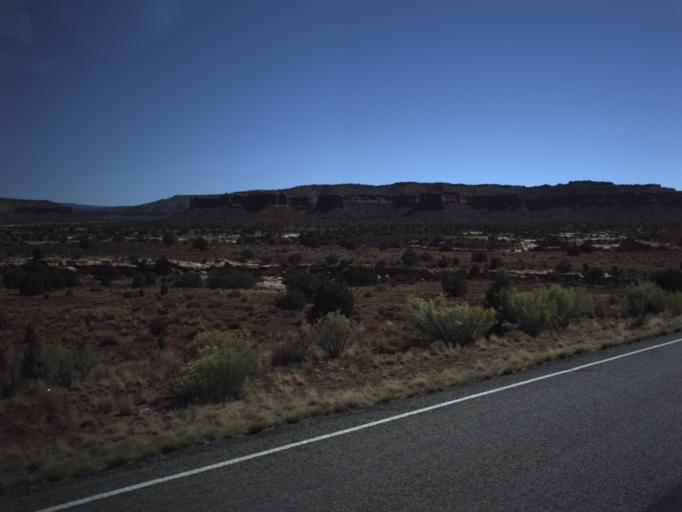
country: US
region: Utah
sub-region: San Juan County
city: Blanding
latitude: 37.7029
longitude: -110.2366
